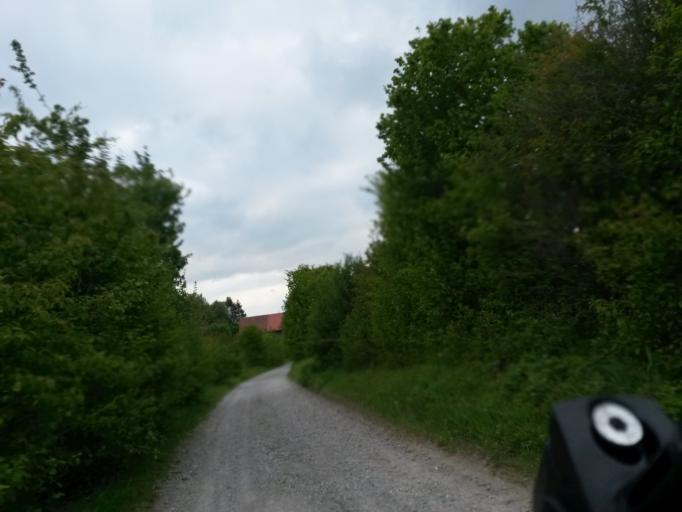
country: DE
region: Baden-Wuerttemberg
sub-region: Tuebingen Region
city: Bad Waldsee
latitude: 47.9340
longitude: 9.7747
